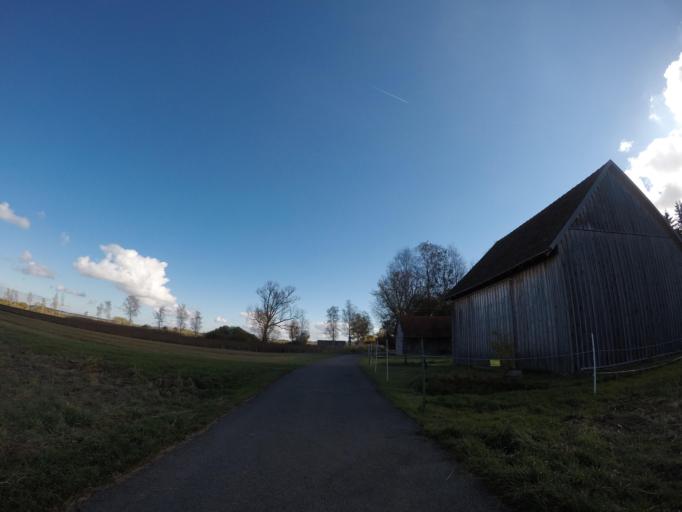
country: DE
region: Baden-Wuerttemberg
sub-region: Tuebingen Region
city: Bad Buchau
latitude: 48.0707
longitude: 9.6087
